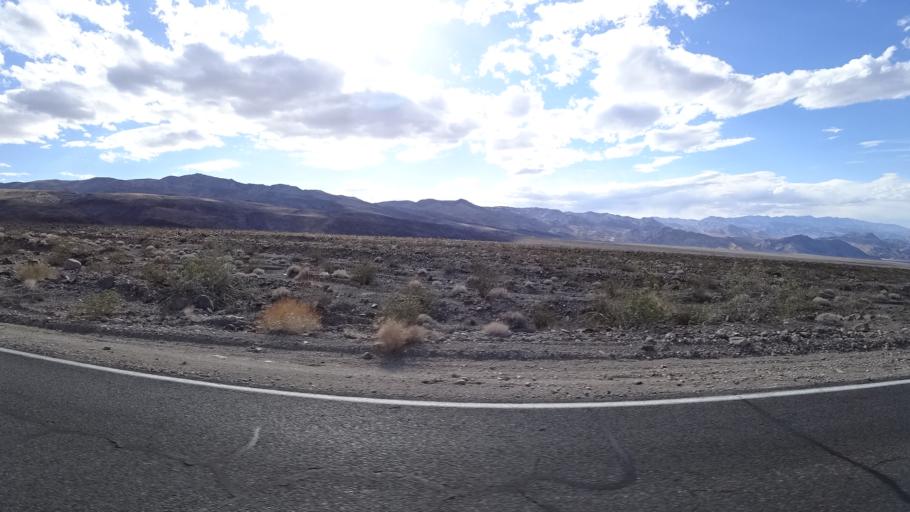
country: US
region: Nevada
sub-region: Nye County
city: Beatty
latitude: 36.4832
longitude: -117.2308
